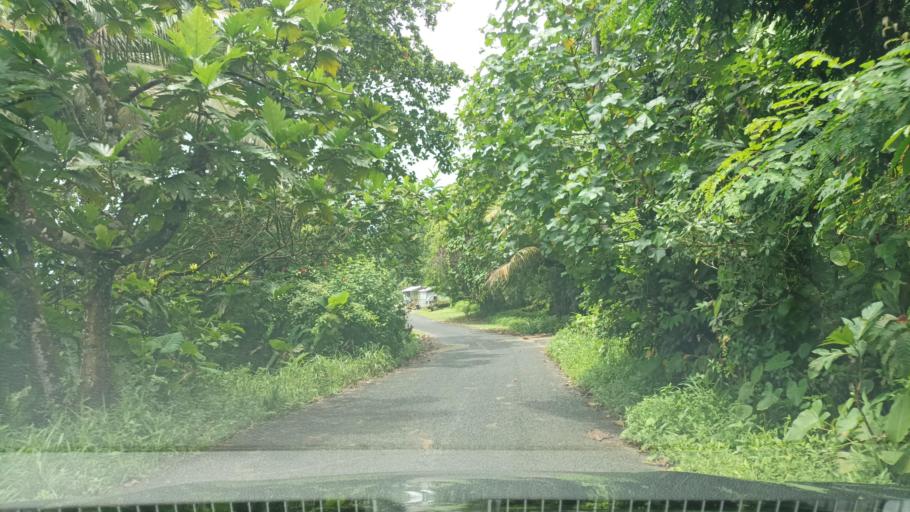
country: FM
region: Pohnpei
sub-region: Kolonia Municipality
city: Kolonia
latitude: 6.9701
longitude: 158.2234
